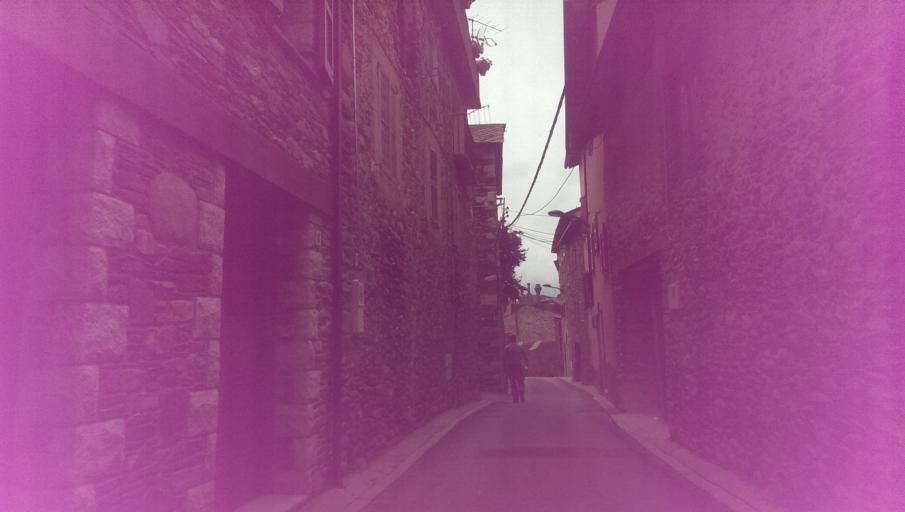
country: ES
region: Catalonia
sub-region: Provincia de Girona
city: Llivia
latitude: 42.4654
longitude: 1.9808
